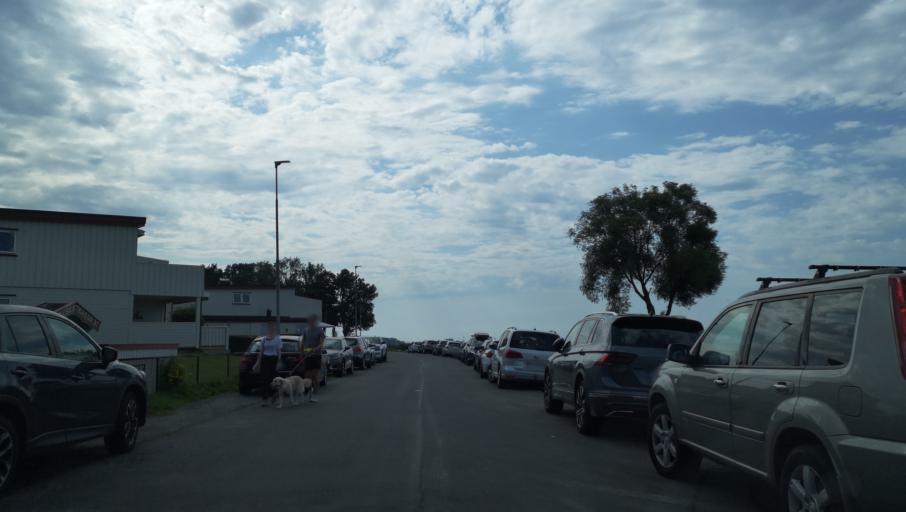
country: NO
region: Ostfold
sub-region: Moss
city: Moss
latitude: 59.4480
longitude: 10.6153
